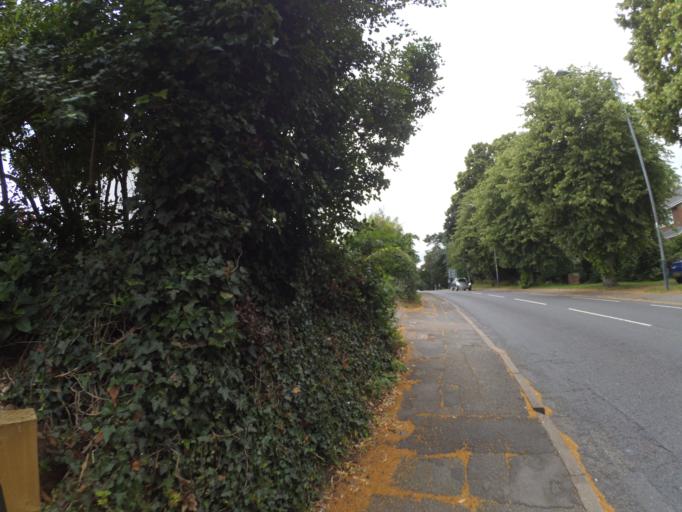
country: GB
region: England
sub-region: Warwickshire
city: Rugby
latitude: 52.3638
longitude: -1.2861
